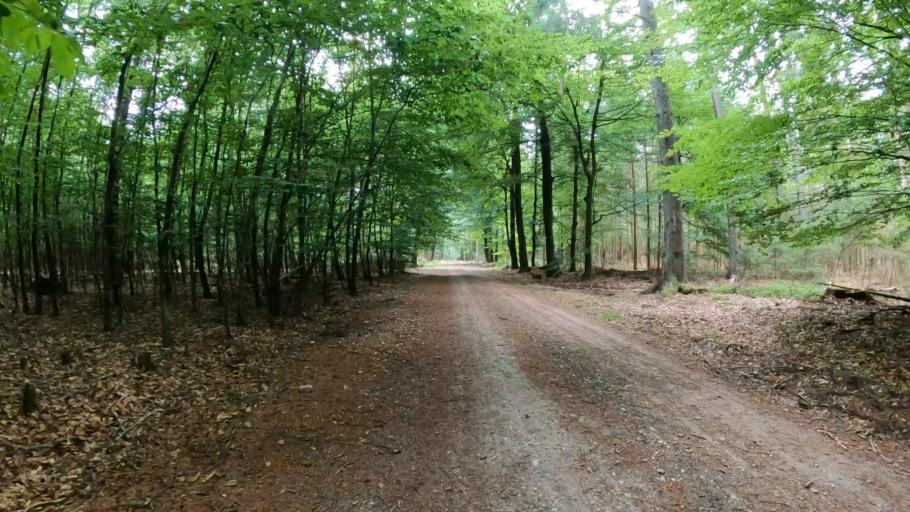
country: DE
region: Schleswig-Holstein
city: Heidmuhlen
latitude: 53.9553
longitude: 10.1075
